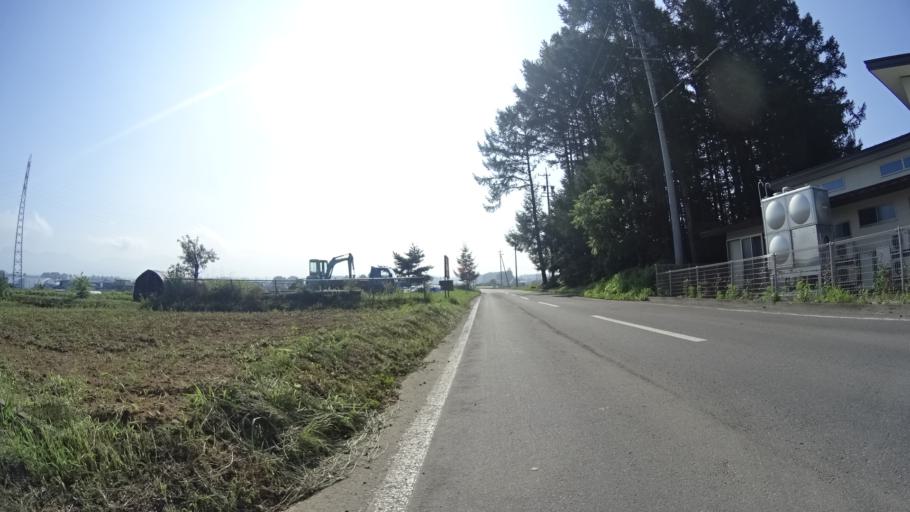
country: JP
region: Nagano
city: Chino
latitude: 35.9670
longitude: 138.1905
